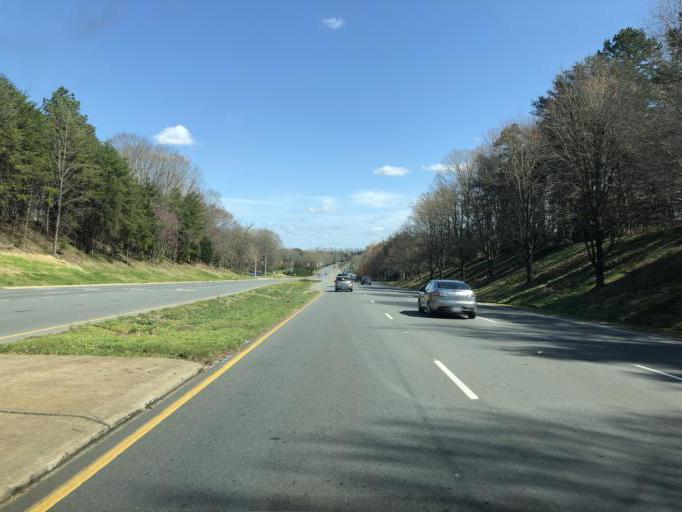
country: US
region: North Carolina
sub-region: Cabarrus County
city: Harrisburg
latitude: 35.3157
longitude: -80.7701
